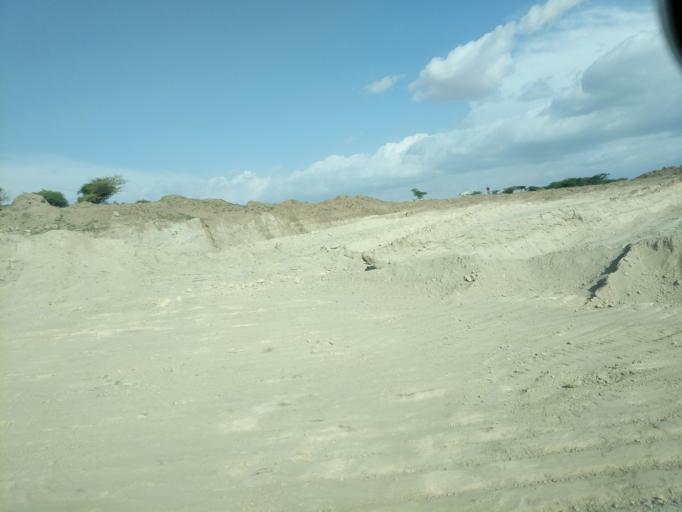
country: ET
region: Oromiya
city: Ziway
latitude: 7.5803
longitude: 38.6829
